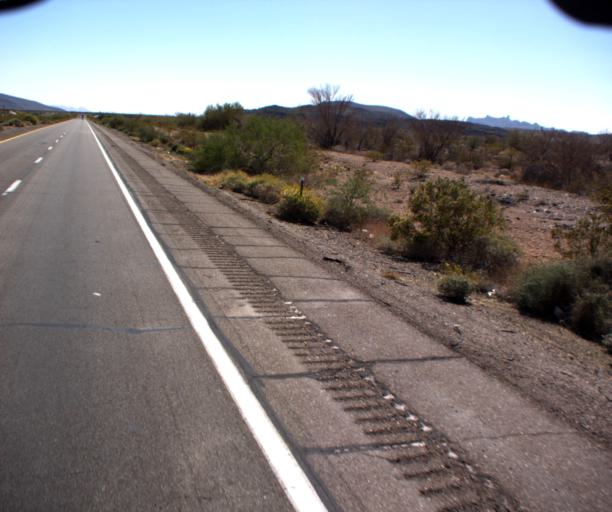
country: US
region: Arizona
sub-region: La Paz County
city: Quartzsite
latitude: 33.6571
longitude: -113.9743
